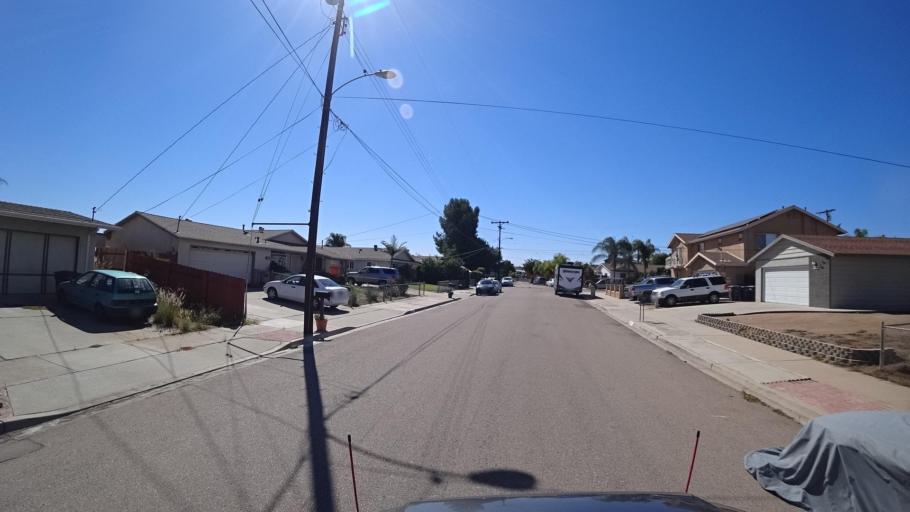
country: US
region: California
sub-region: San Diego County
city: La Presa
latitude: 32.6972
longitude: -117.0077
